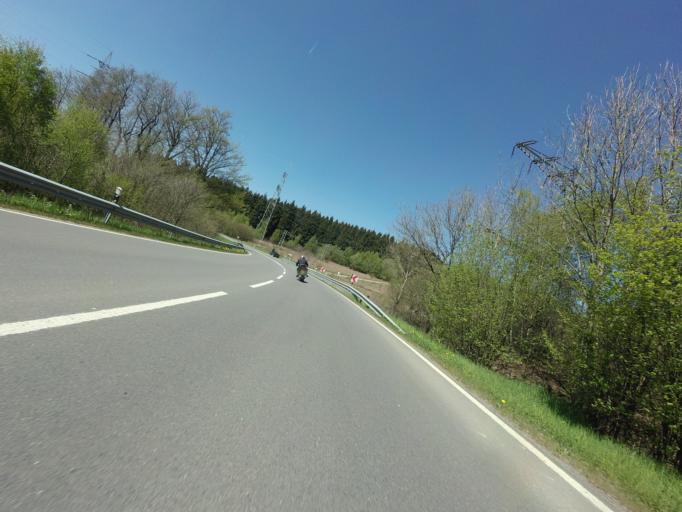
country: DE
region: North Rhine-Westphalia
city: Kreuztal
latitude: 51.0129
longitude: 7.9409
